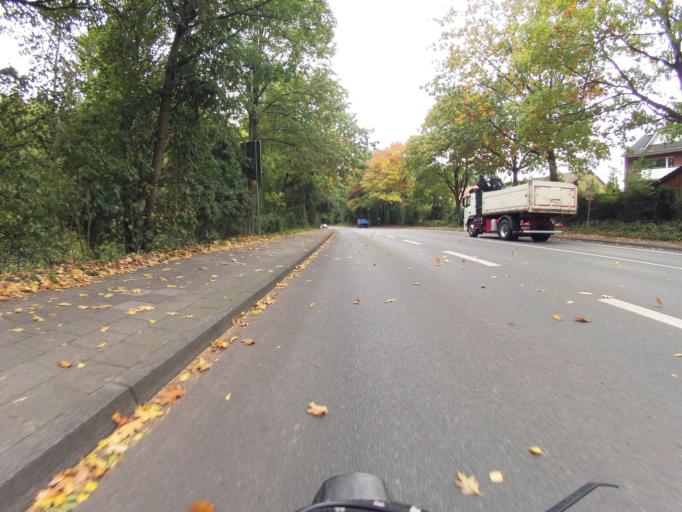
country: DE
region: North Rhine-Westphalia
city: Ibbenburen
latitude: 52.2880
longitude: 7.7243
